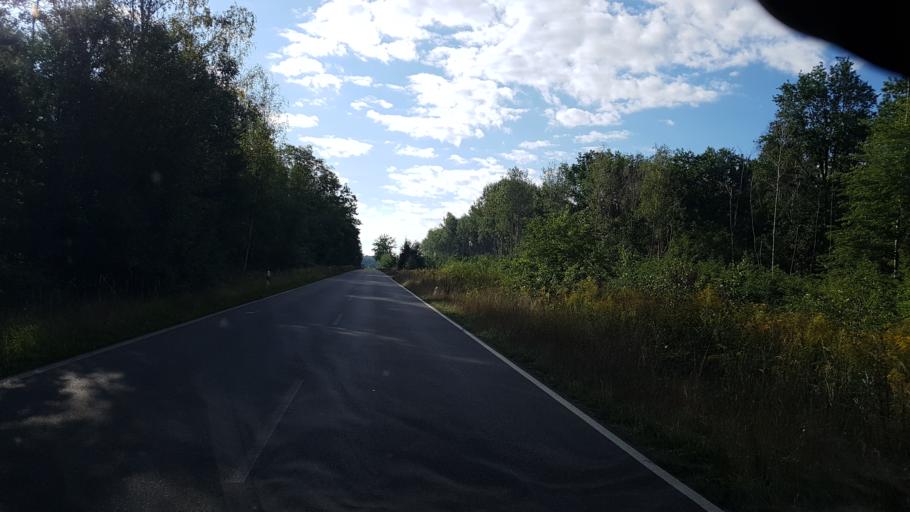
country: DE
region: Brandenburg
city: Welzow
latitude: 51.5371
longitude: 14.2395
